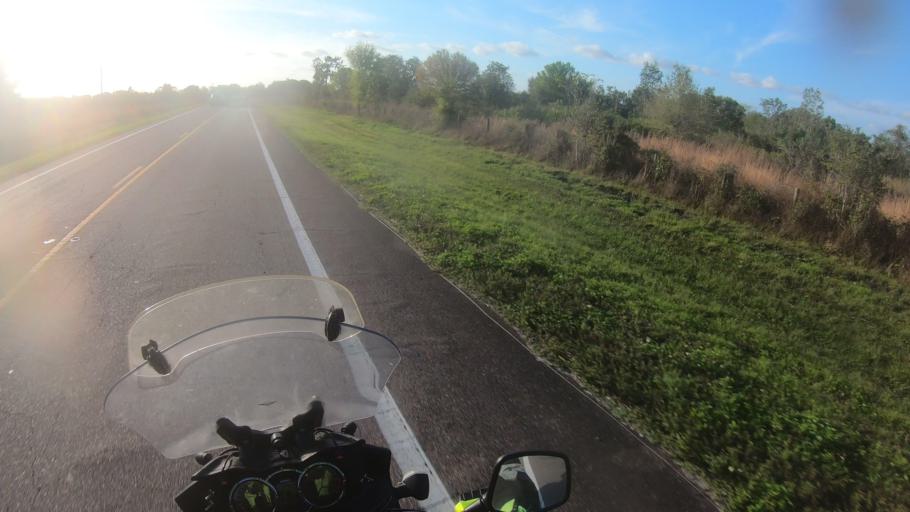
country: US
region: Florida
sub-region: DeSoto County
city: Arcadia
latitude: 27.2964
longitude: -82.0680
